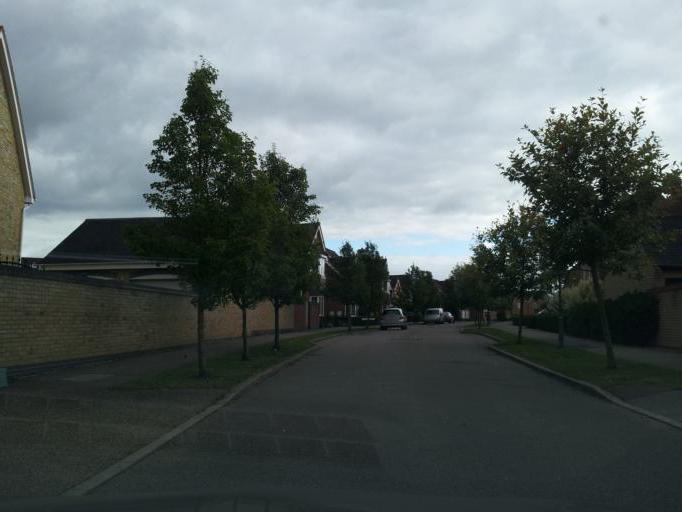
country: GB
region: England
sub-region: Milton Keynes
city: Shenley Church End
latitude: 52.0014
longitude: -0.8071
